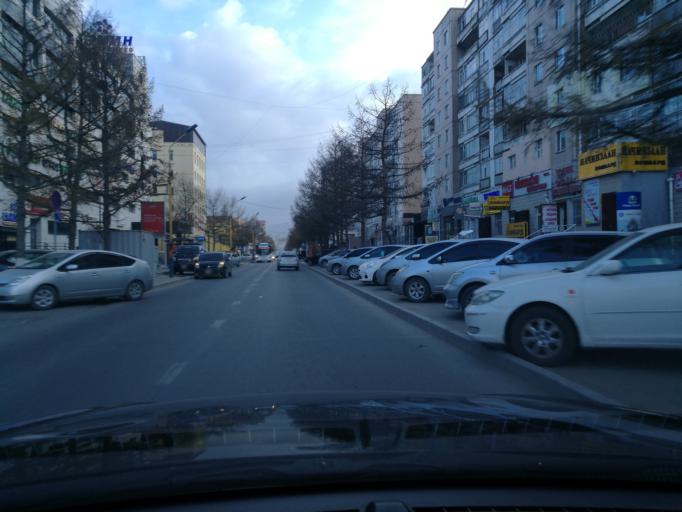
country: MN
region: Ulaanbaatar
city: Ulaanbaatar
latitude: 47.9283
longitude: 106.9267
